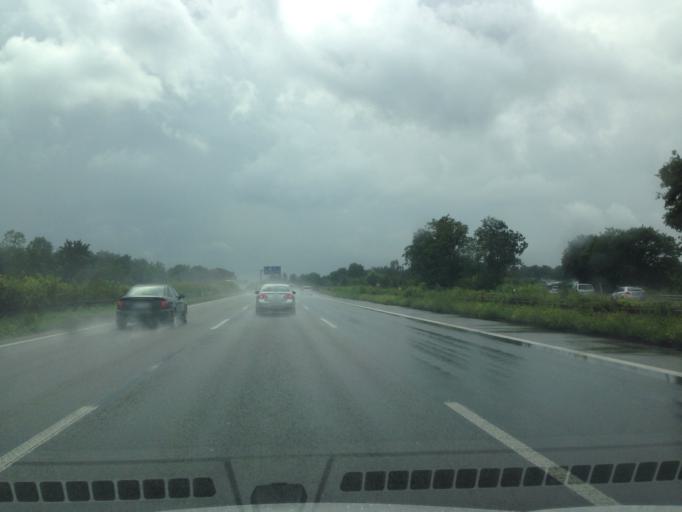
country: DE
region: North Rhine-Westphalia
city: Meiderich
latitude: 51.4900
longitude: 6.8160
